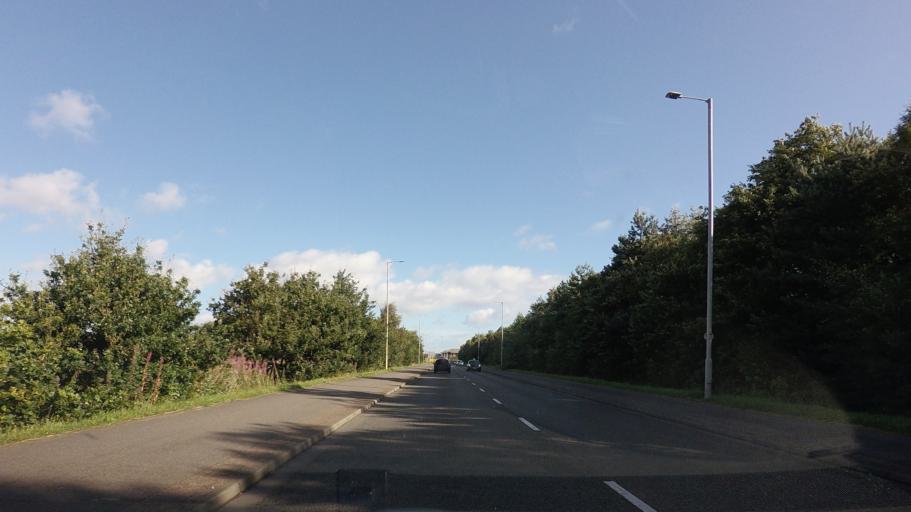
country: GB
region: Scotland
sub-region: Highland
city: Inverness
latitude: 57.4684
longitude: -4.1928
